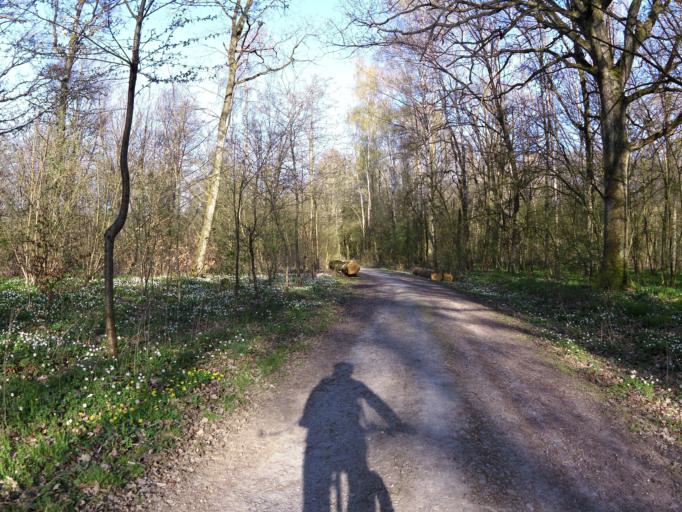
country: DE
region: Bavaria
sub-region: Regierungsbezirk Unterfranken
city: Kurnach
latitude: 49.8271
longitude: 10.0641
